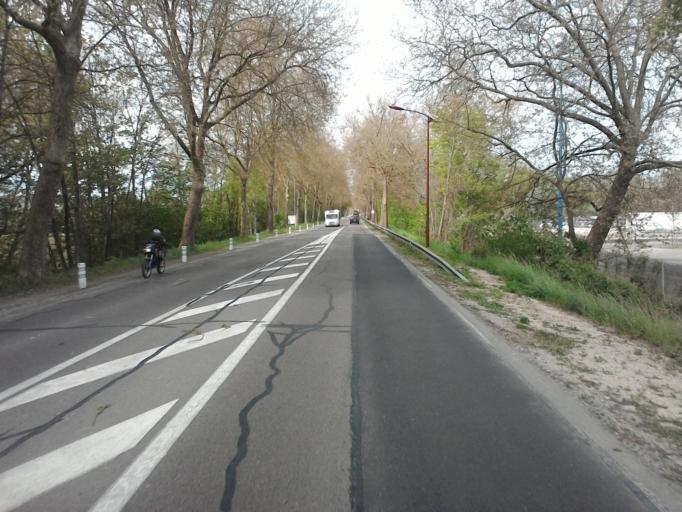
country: FR
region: Bourgogne
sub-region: Departement de l'Yonne
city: Saint-Florentin
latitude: 47.9868
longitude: 3.7333
